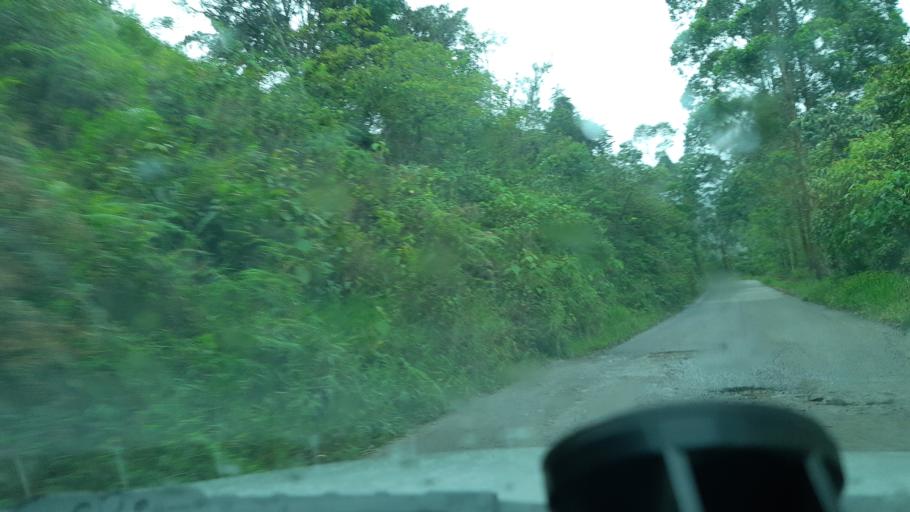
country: CO
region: Boyaca
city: Chinavita
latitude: 5.1917
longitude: -73.3816
